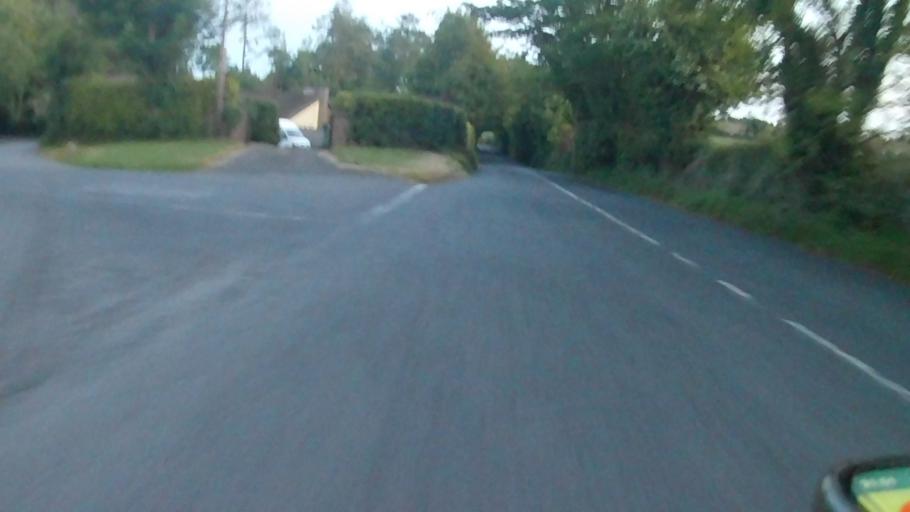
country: IE
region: Munster
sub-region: County Cork
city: Carrigtwohill
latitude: 51.9575
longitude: -8.3042
